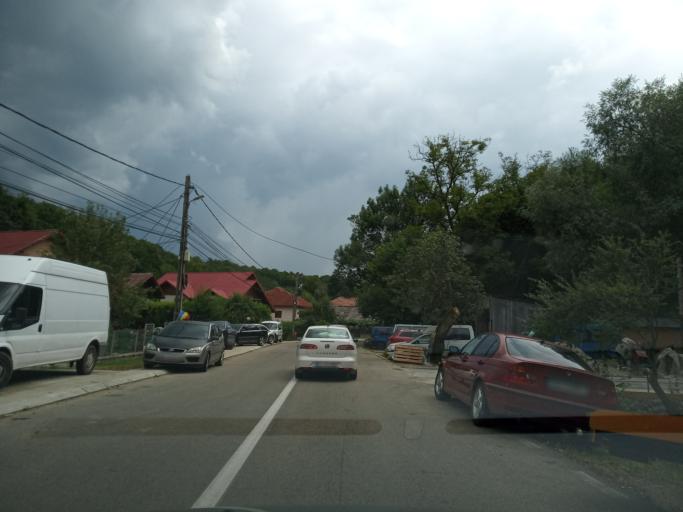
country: RO
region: Gorj
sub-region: Comuna Tismana
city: Pocruia
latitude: 45.0684
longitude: 22.9403
